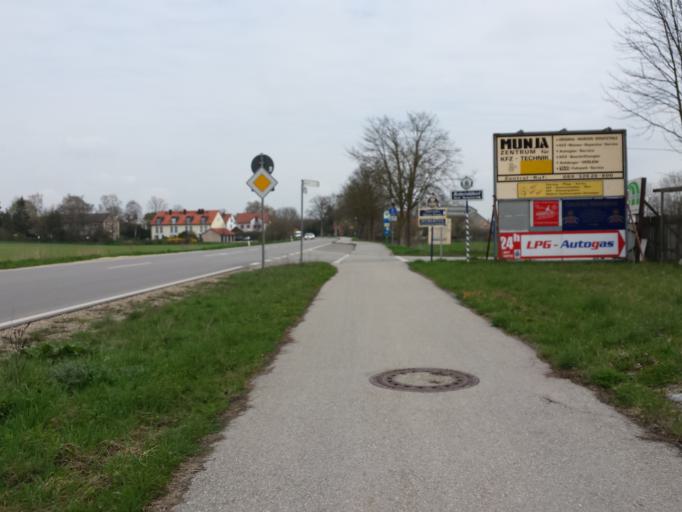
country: DE
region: Bavaria
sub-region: Upper Bavaria
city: Garching bei Munchen
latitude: 48.2284
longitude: 11.6408
